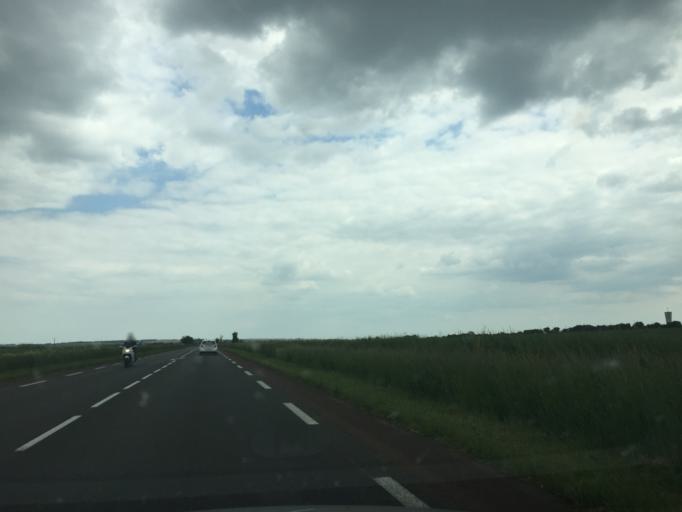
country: FR
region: Pays de la Loire
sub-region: Departement de la Vendee
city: Benet
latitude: 46.3812
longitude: -0.6080
